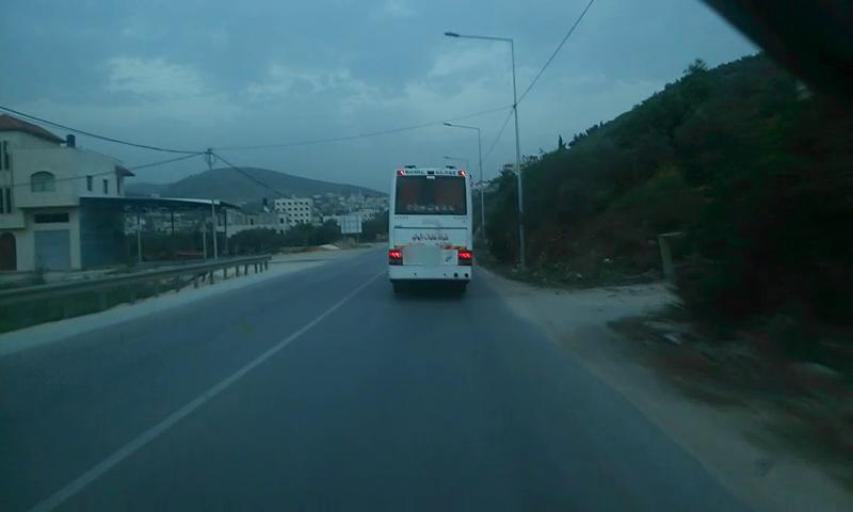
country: PS
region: West Bank
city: Kafr al Labad
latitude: 32.3109
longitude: 35.1043
